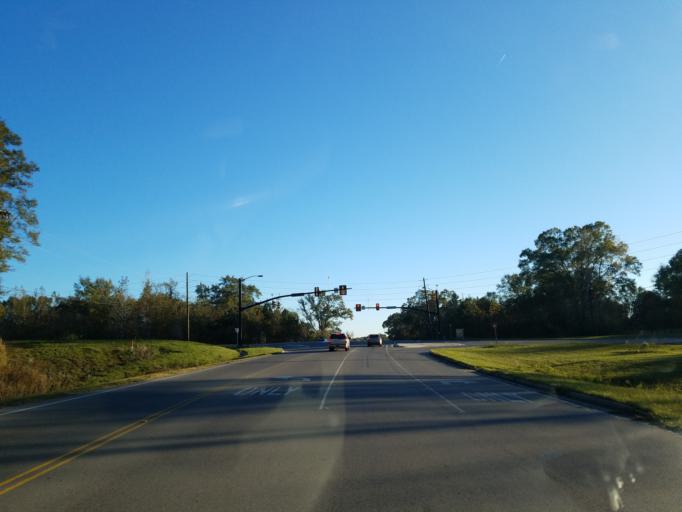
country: US
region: Mississippi
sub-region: Lamar County
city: Arnold Line
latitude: 31.3393
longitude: -89.3986
